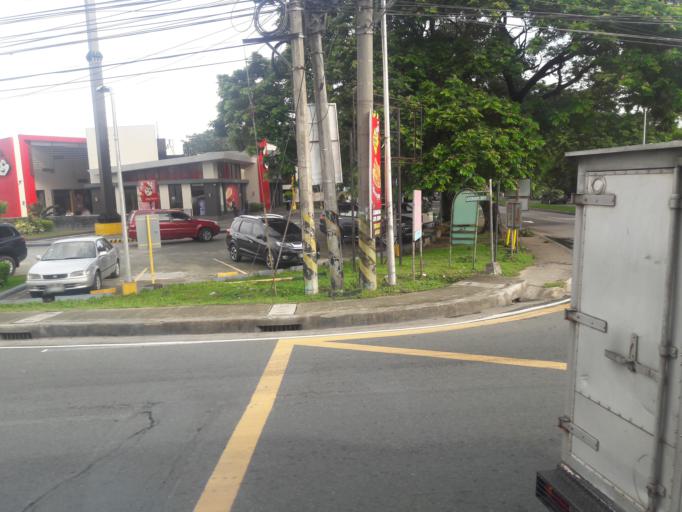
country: PH
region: Calabarzon
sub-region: Province of Cavite
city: Carmona
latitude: 14.3111
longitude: 121.0417
